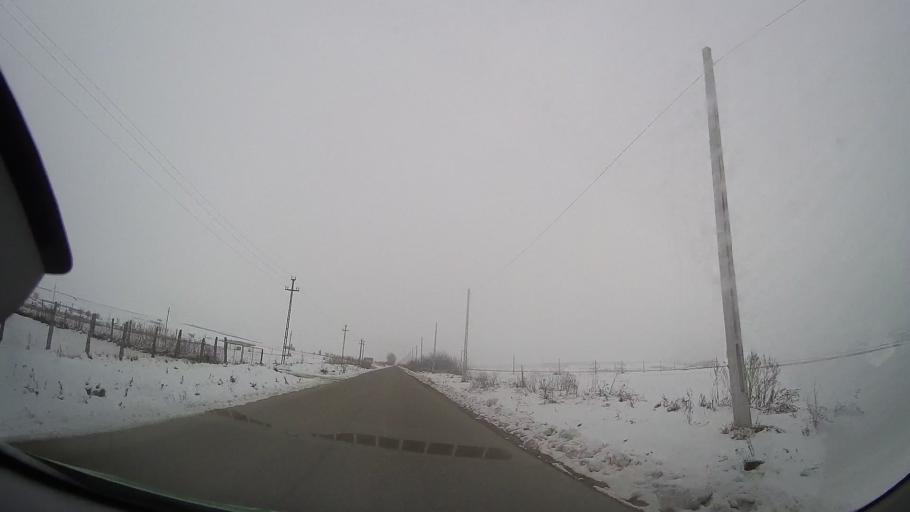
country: RO
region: Vaslui
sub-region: Comuna Todiresti
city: Todiresti
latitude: 46.8407
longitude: 27.3978
